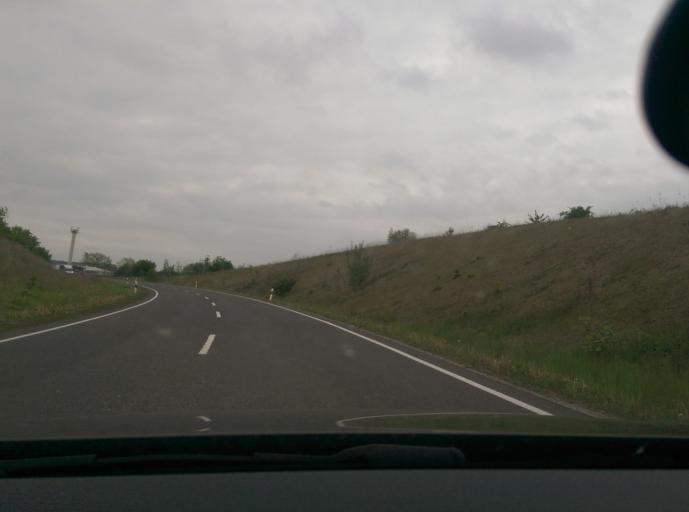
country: DE
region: Thuringia
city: Krauthausen
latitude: 51.0157
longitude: 10.2597
